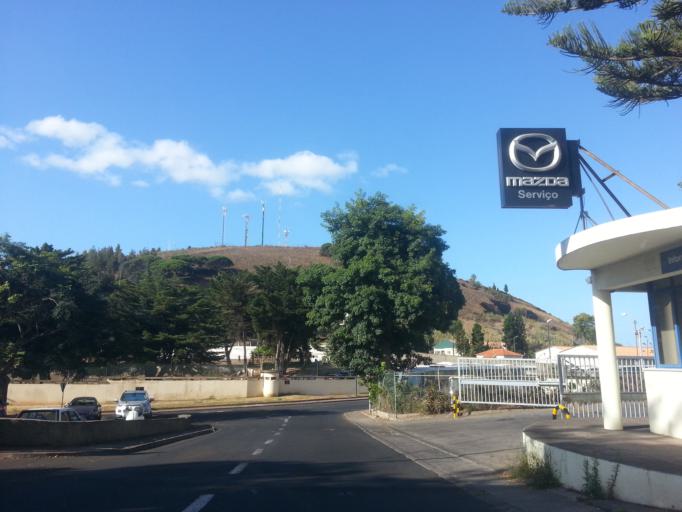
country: PT
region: Madeira
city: Camara de Lobos
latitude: 32.6453
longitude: -16.9373
